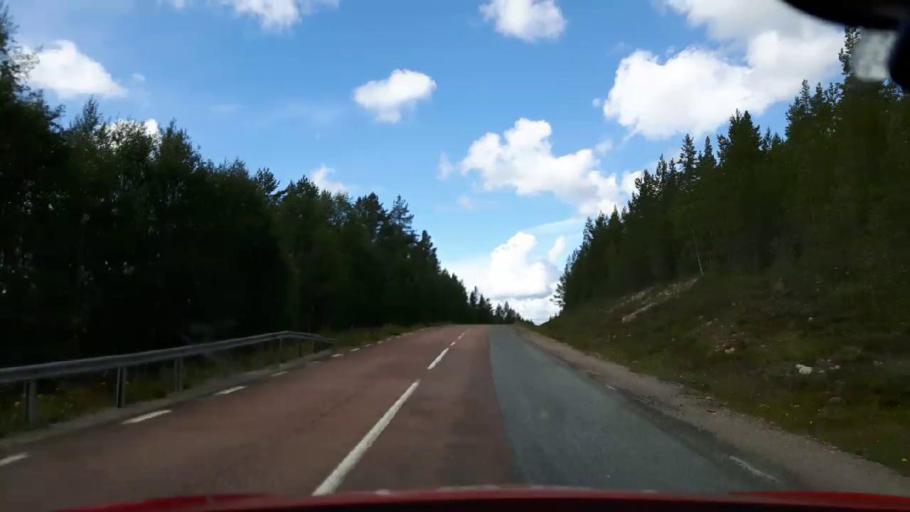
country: SE
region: Dalarna
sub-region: Alvdalens Kommun
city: AElvdalen
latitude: 61.7982
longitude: 13.6867
